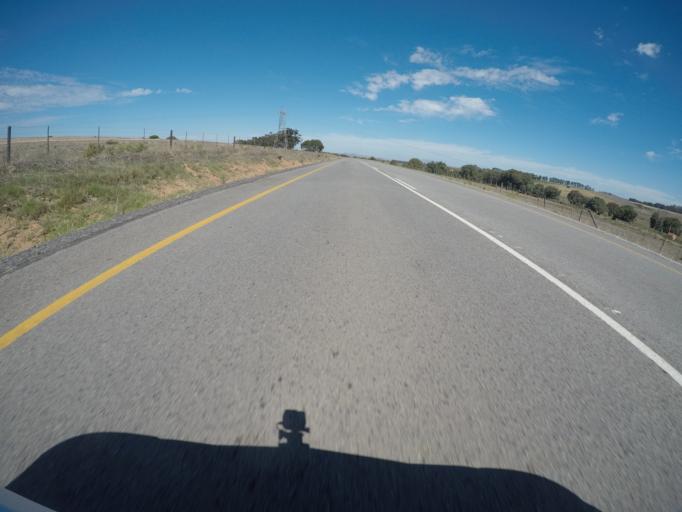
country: ZA
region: Western Cape
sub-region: West Coast District Municipality
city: Malmesbury
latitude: -33.5015
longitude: 18.6799
